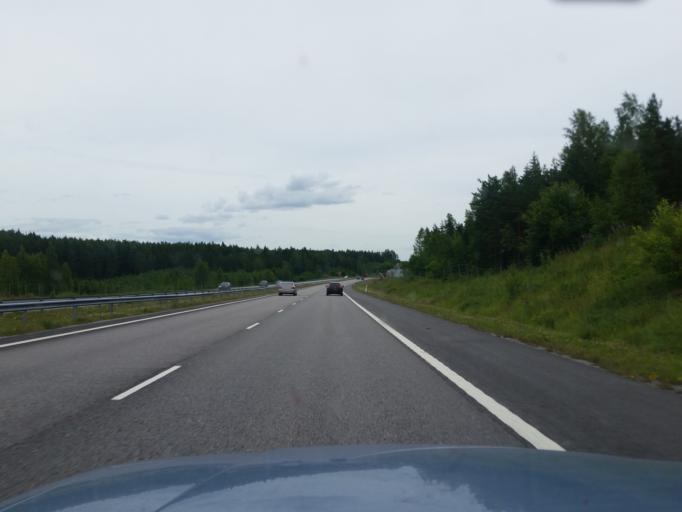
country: FI
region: Varsinais-Suomi
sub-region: Salo
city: Halikko
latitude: 60.4344
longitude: 22.9755
